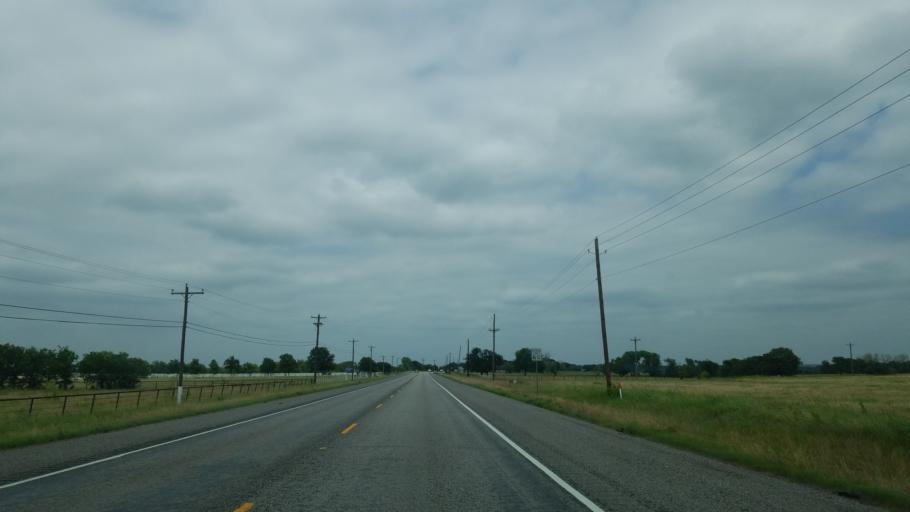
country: US
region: Texas
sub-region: Denton County
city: Denton
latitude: 33.2728
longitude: -97.0988
